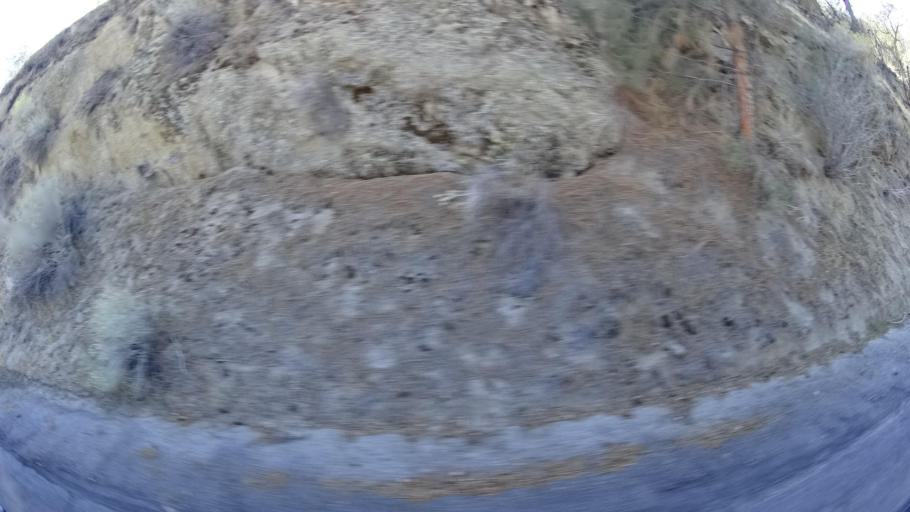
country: US
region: California
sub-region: Kern County
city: Bodfish
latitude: 35.5752
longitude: -118.5503
